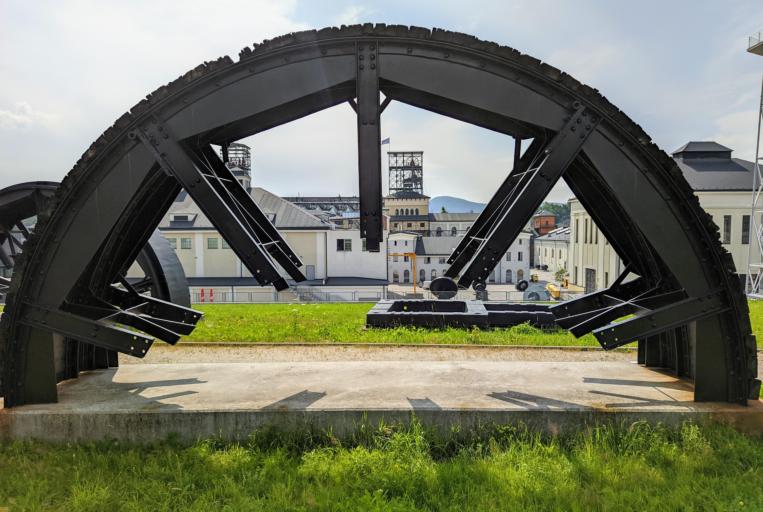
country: PL
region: Lower Silesian Voivodeship
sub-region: Powiat walbrzyski
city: Walbrzych
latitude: 50.7729
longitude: 16.2604
